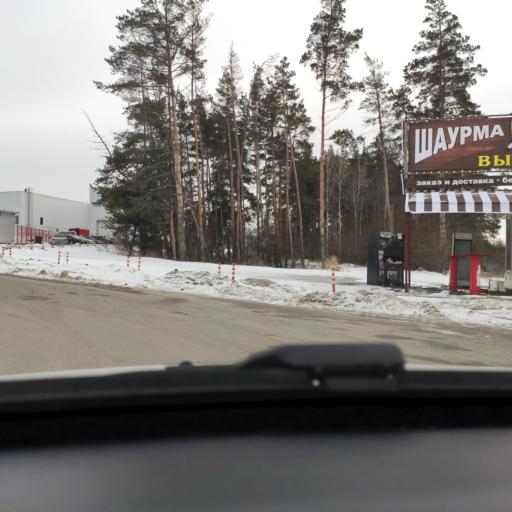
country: RU
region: Voronezj
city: Ramon'
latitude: 51.9323
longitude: 39.2121
